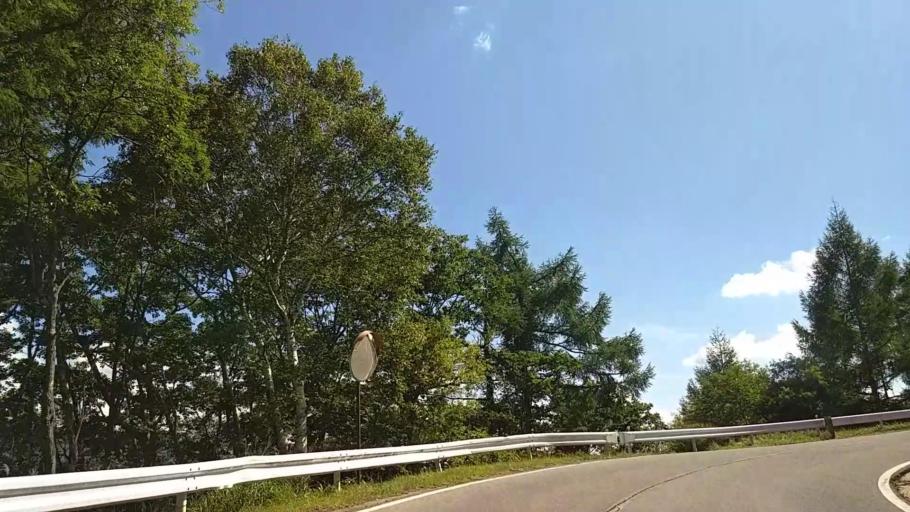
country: JP
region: Nagano
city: Chino
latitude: 36.0820
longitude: 138.2874
